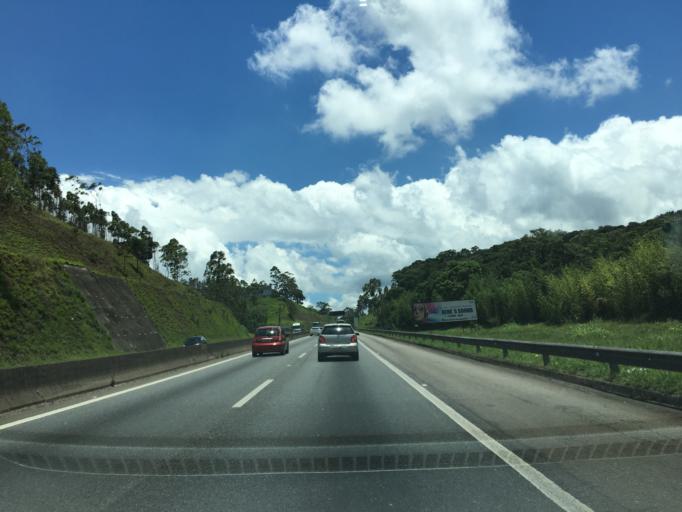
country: BR
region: Sao Paulo
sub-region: Mairipora
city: Mairipora
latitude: -23.2770
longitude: -46.5858
